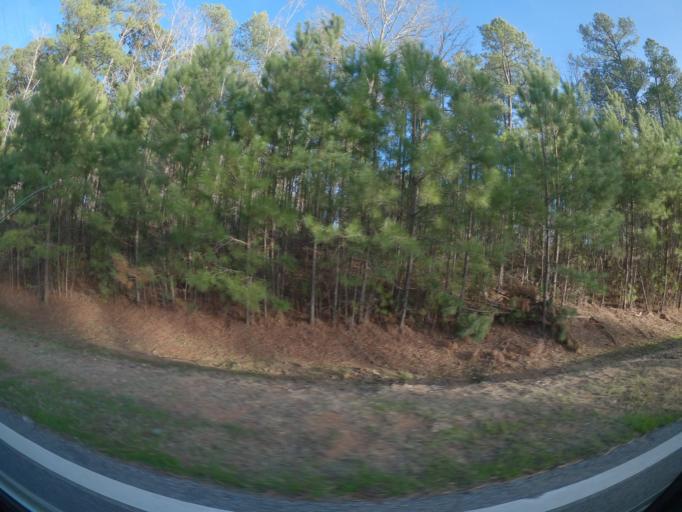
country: US
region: Georgia
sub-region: Columbia County
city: Evans
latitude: 33.5828
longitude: -82.2005
